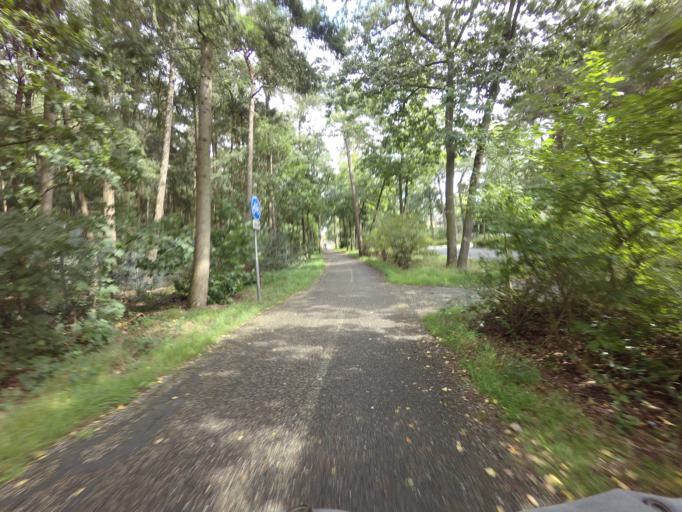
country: NL
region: Utrecht
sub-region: Gemeente Zeist
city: Zeist
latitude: 52.0965
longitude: 5.2319
